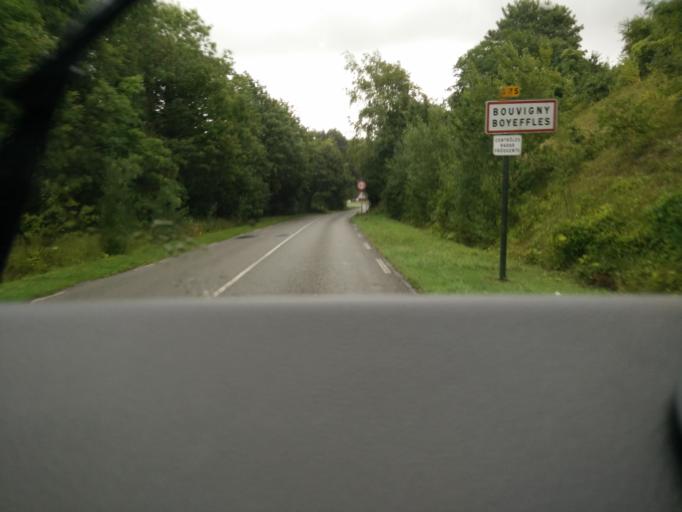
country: FR
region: Nord-Pas-de-Calais
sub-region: Departement du Pas-de-Calais
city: Bouvigny-Boyeffles
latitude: 50.4215
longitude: 2.6567
